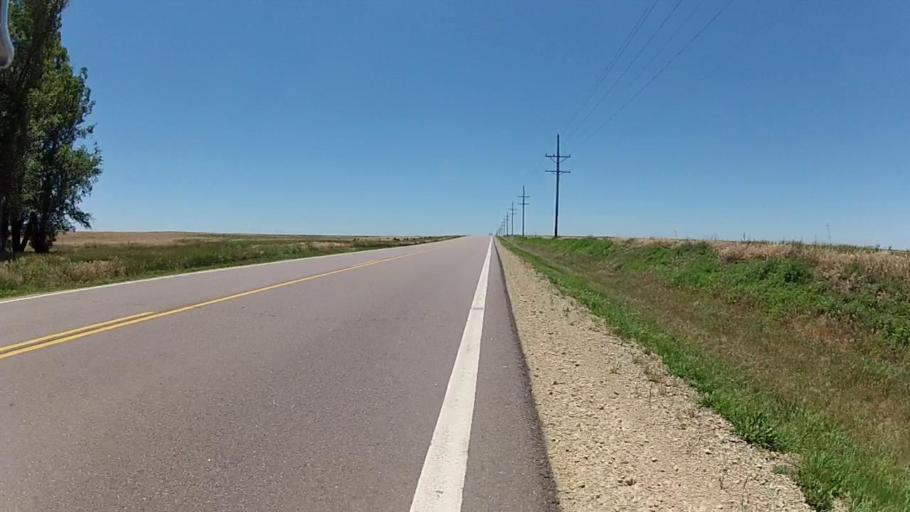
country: US
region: Kansas
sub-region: Kiowa County
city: Greensburg
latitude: 37.5396
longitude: -99.3210
